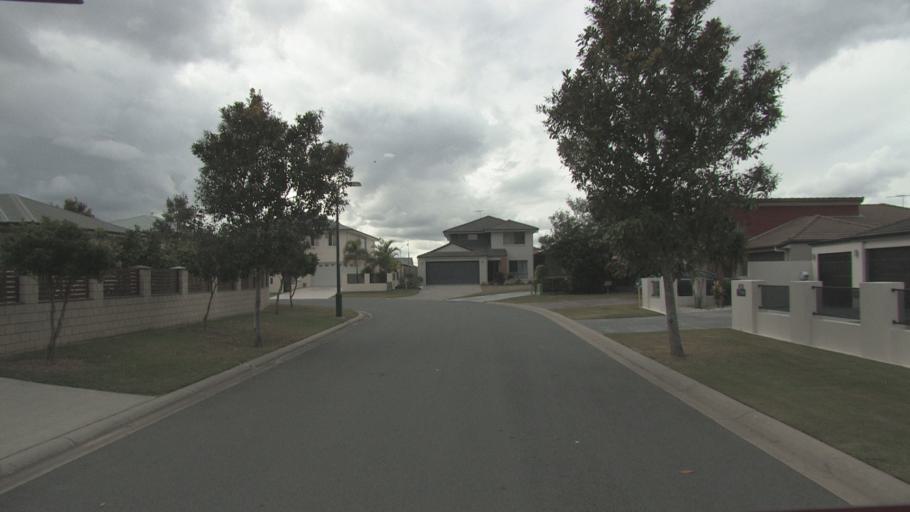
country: AU
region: Queensland
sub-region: Logan
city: Park Ridge South
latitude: -27.6825
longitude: 153.0458
